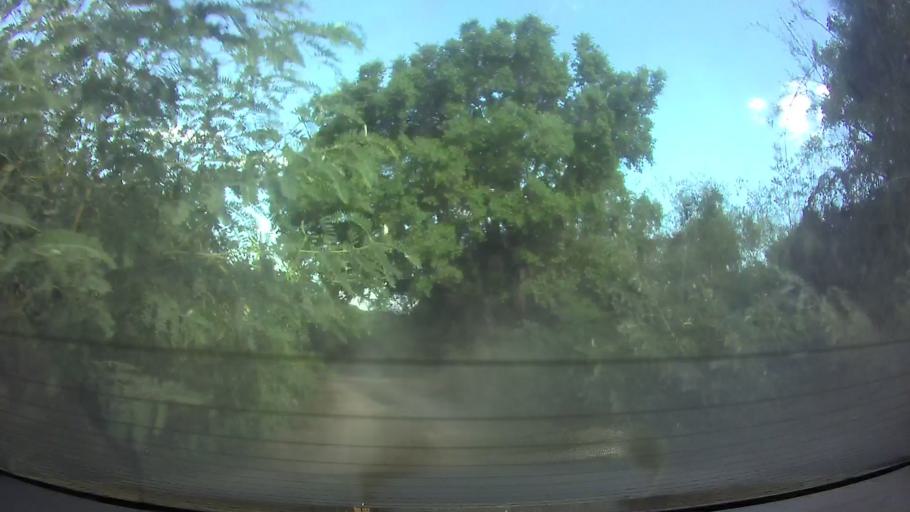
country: PY
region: Cordillera
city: Arroyos y Esteros
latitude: -24.9703
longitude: -57.1920
